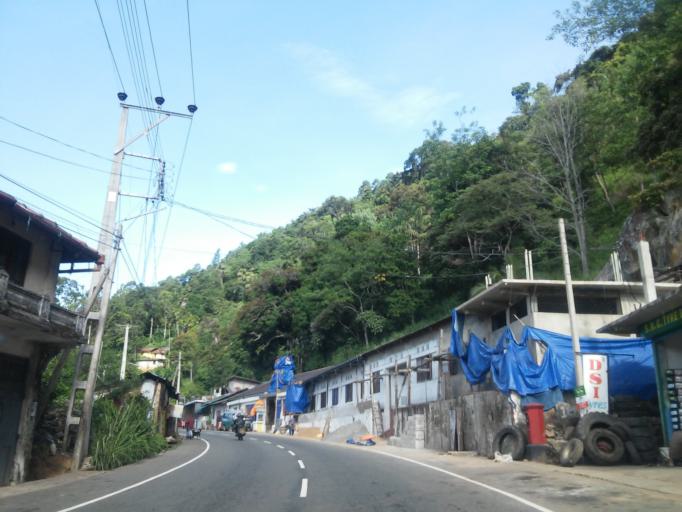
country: LK
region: Uva
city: Haputale
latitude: 6.7657
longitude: 80.8897
